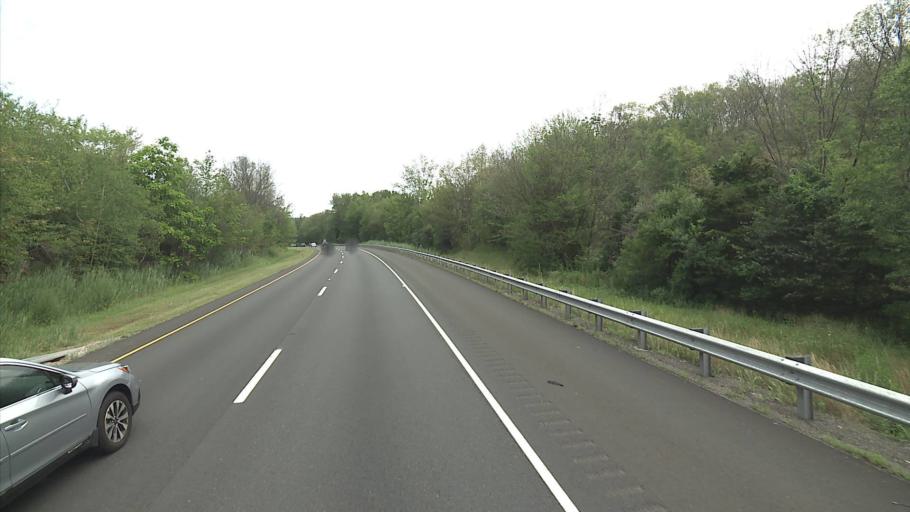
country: US
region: Connecticut
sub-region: New Haven County
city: Middlebury
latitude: 41.5262
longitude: -73.0883
